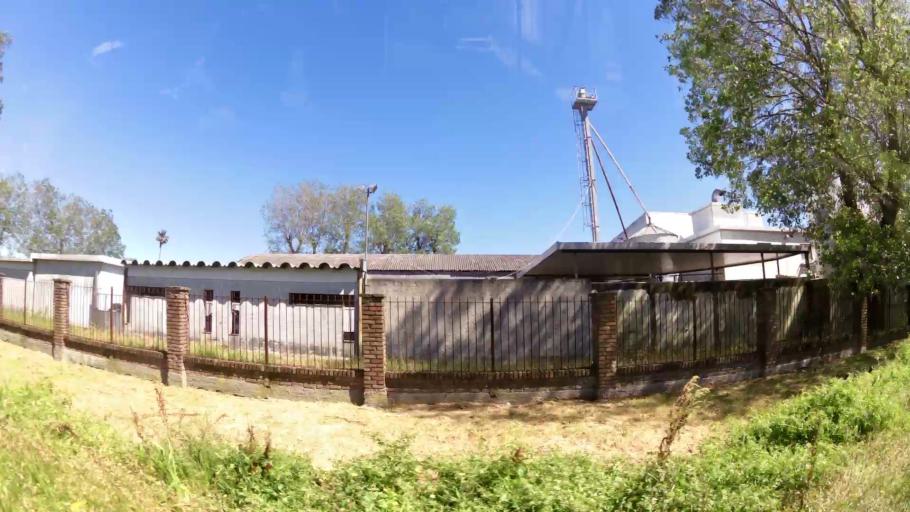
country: UY
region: Canelones
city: Paso de Carrasco
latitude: -34.8642
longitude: -56.1164
